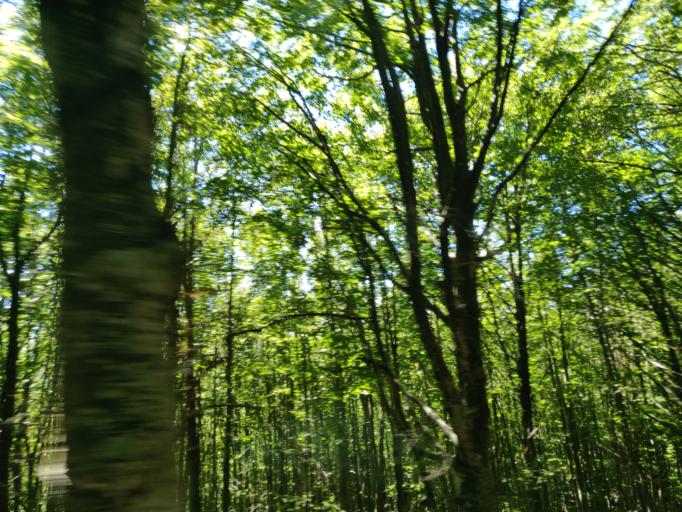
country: IT
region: Tuscany
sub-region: Provincia di Siena
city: Abbadia San Salvatore
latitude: 42.8850
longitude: 11.6244
